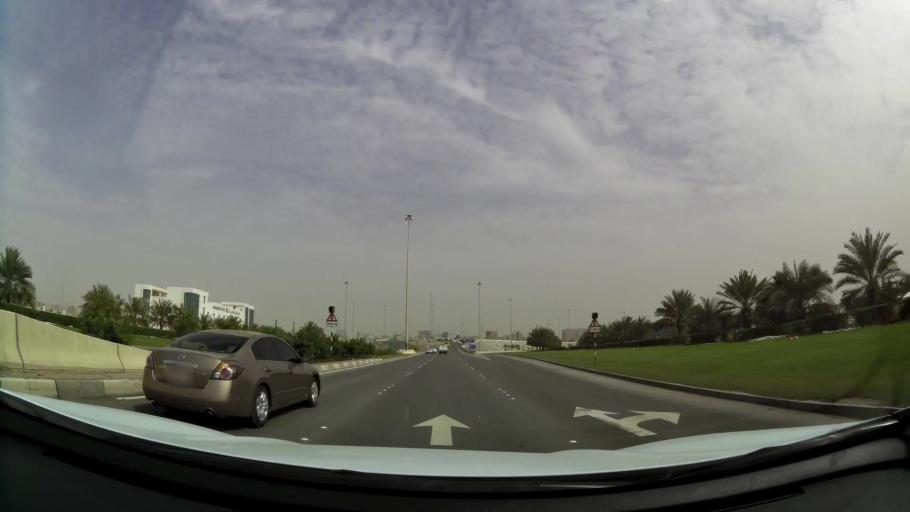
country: AE
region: Abu Dhabi
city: Abu Dhabi
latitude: 24.3240
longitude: 54.5220
